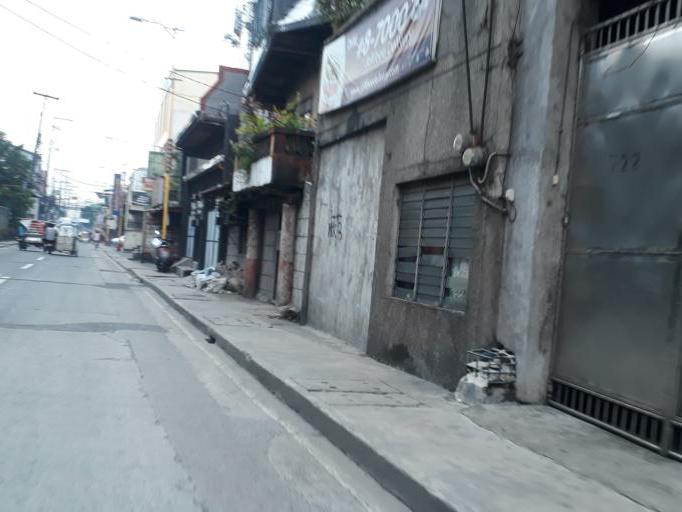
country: PH
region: Metro Manila
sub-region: Caloocan City
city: Niugan
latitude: 14.6538
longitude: 120.9492
